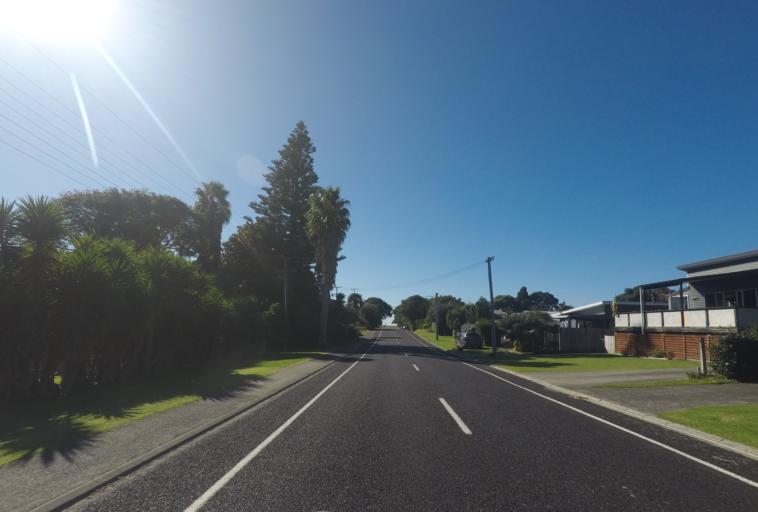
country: NZ
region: Waikato
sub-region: Thames-Coromandel District
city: Whangamata
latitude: -37.2833
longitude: 175.8994
